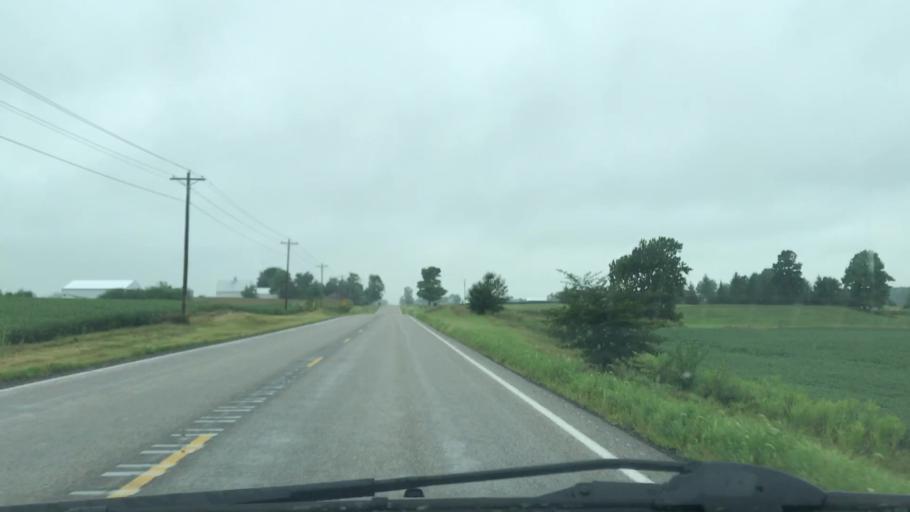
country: US
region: Indiana
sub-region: Boone County
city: Lebanon
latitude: 40.1264
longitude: -86.4380
